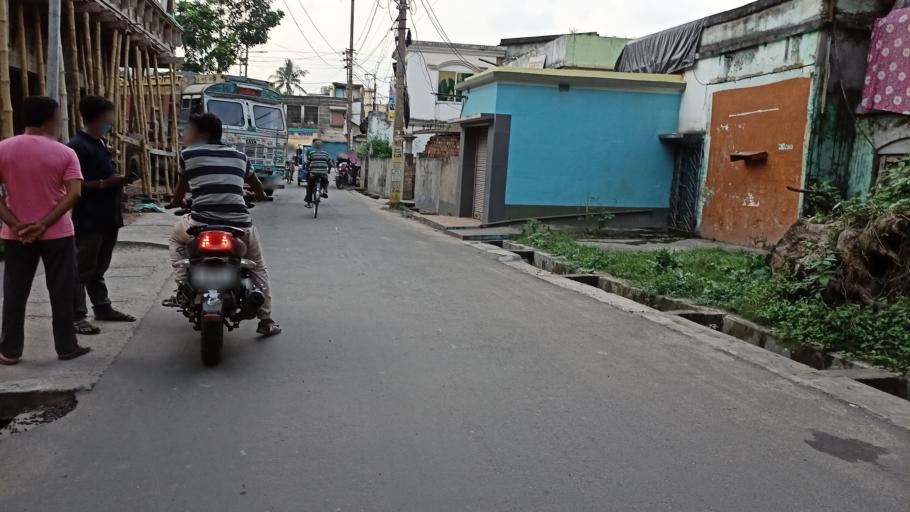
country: IN
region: West Bengal
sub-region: North 24 Parganas
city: Bangaon
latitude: 23.0476
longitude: 88.8255
